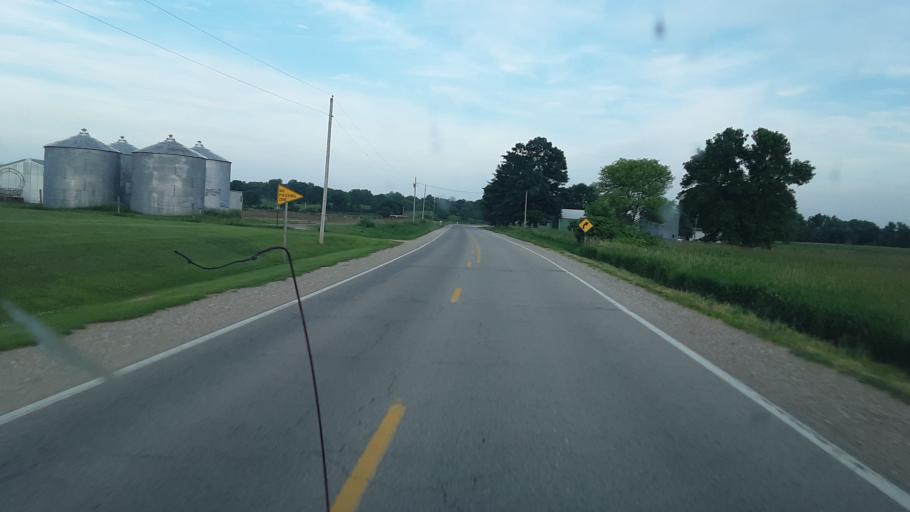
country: US
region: Iowa
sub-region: Benton County
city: Belle Plaine
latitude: 41.9363
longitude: -92.4050
